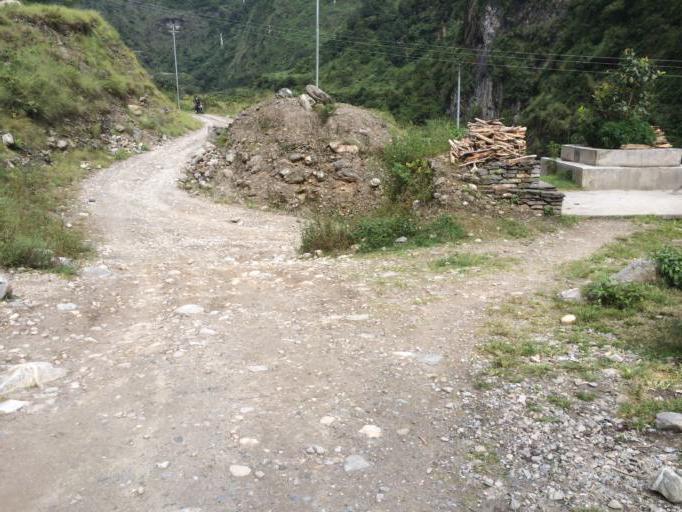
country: NP
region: Western Region
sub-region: Dhawalagiri Zone
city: Chitre
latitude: 28.5161
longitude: 83.6616
